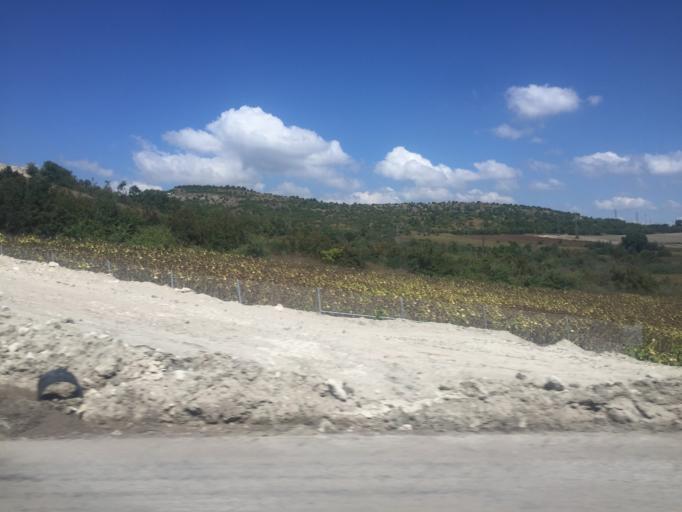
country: TR
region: Balikesir
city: Gobel
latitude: 39.9763
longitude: 28.1694
